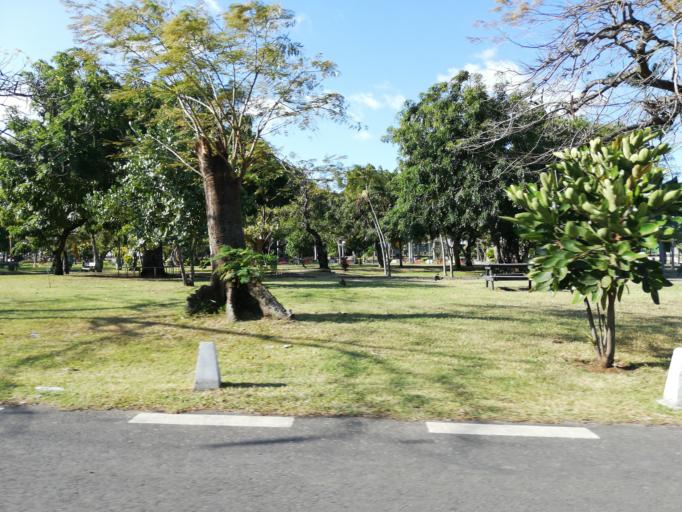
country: MU
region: Port Louis
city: Port Louis
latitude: -20.1591
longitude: 57.4881
